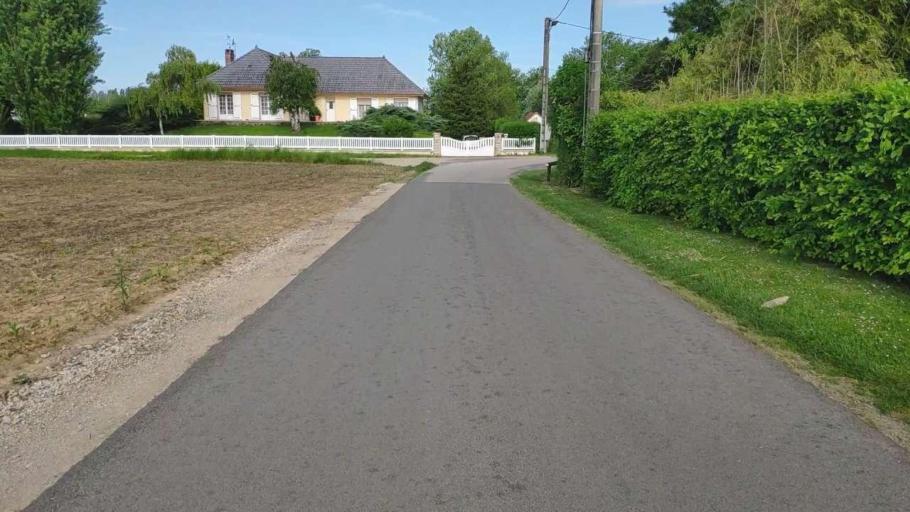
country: FR
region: Franche-Comte
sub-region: Departement du Jura
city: Bletterans
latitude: 46.7323
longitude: 5.4576
